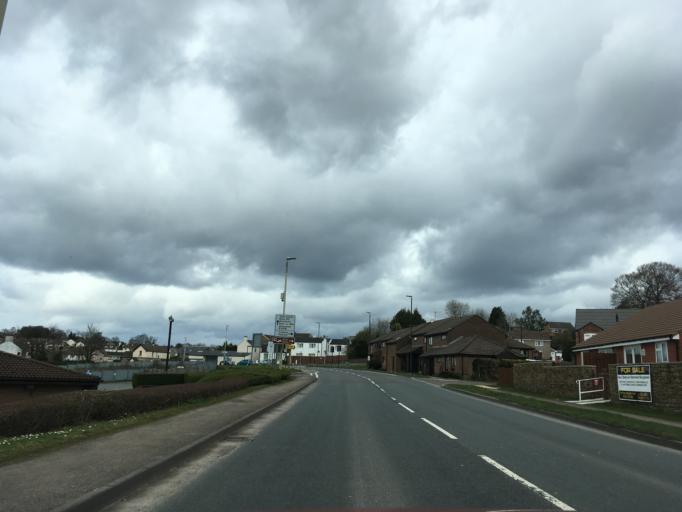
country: GB
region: England
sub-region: Gloucestershire
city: Coleford
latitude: 51.7916
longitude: -2.6143
